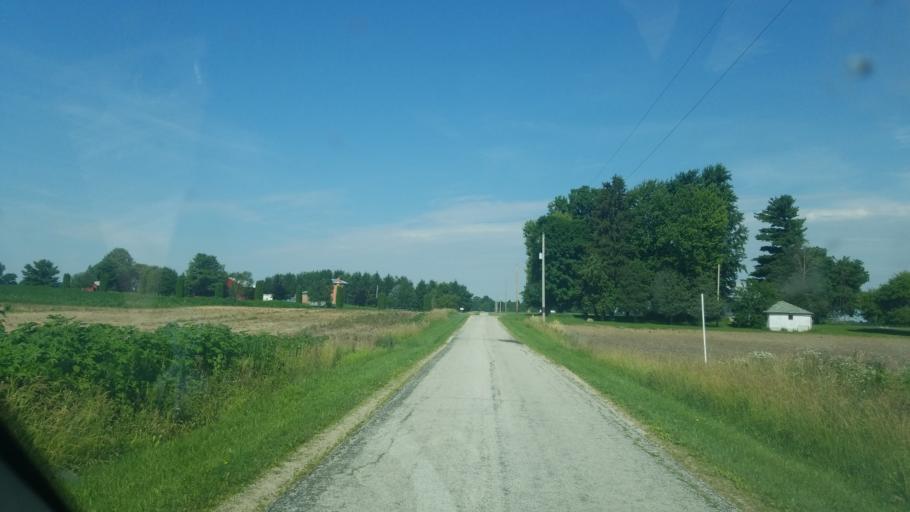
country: US
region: Ohio
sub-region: Wyandot County
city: Upper Sandusky
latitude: 40.9203
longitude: -83.2223
